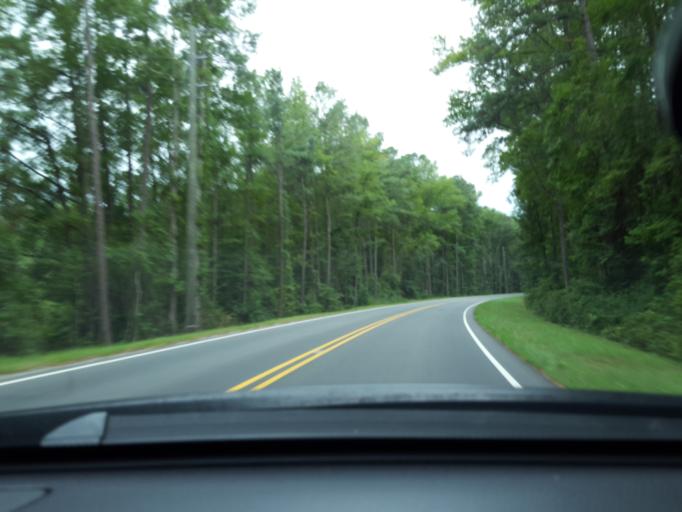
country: US
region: North Carolina
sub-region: Sampson County
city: Roseboro
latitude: 34.7654
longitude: -78.4042
